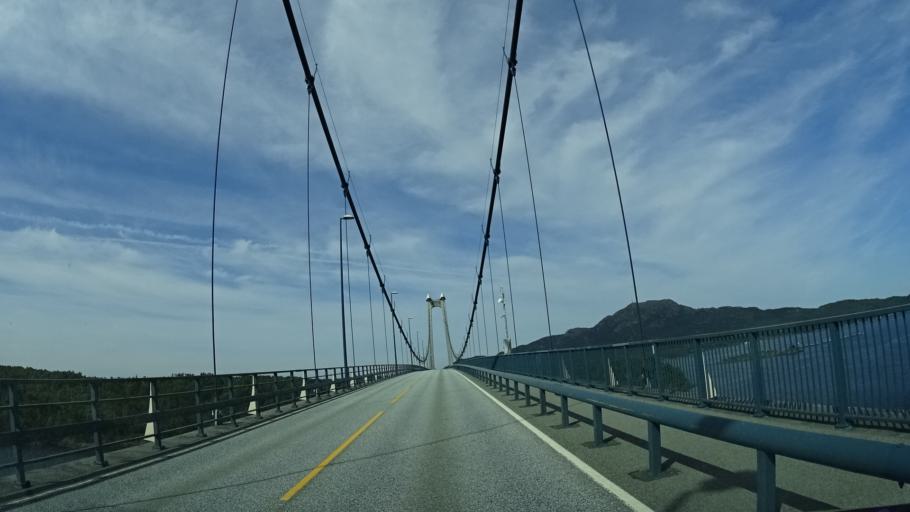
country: NO
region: Hordaland
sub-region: Bomlo
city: Mosterhamn
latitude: 59.7372
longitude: 5.3806
